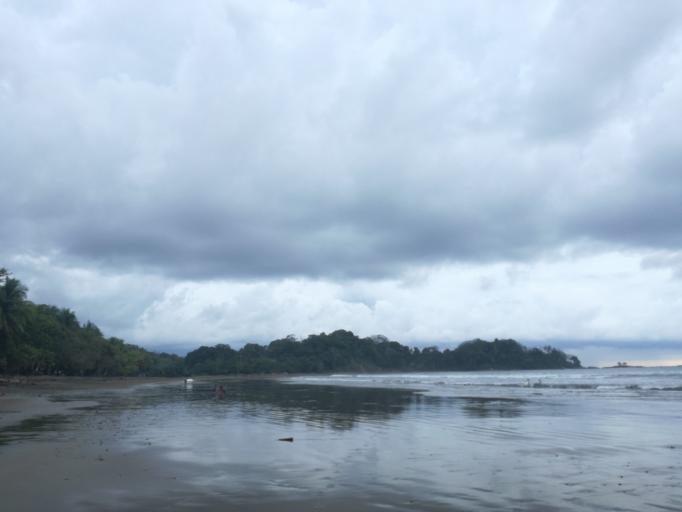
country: CR
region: San Jose
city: San Isidro
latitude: 9.2328
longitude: -83.8420
